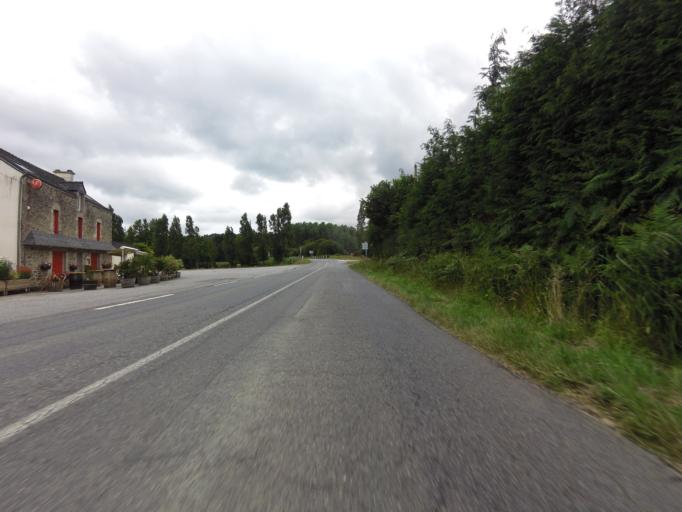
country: FR
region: Brittany
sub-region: Departement du Morbihan
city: Pluherlin
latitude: 47.7119
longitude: -2.3363
